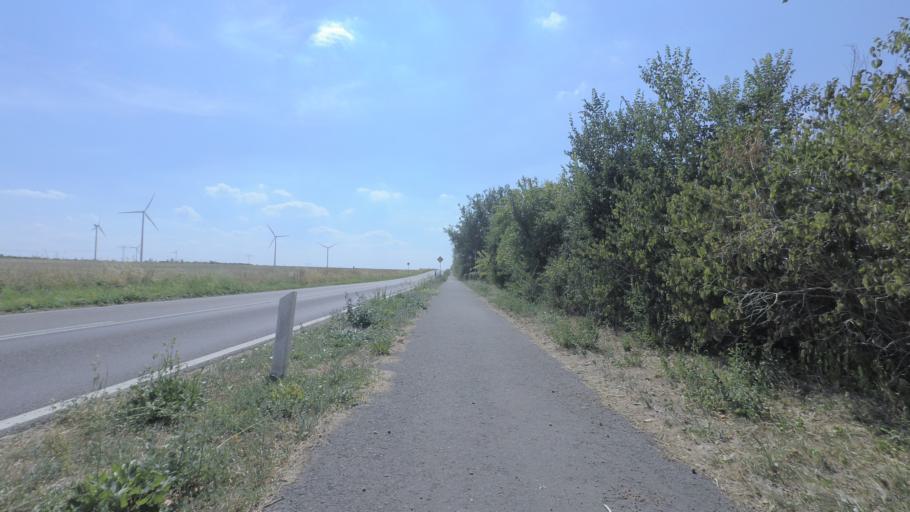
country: DE
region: Brandenburg
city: Trebbin
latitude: 52.2103
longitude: 13.2821
